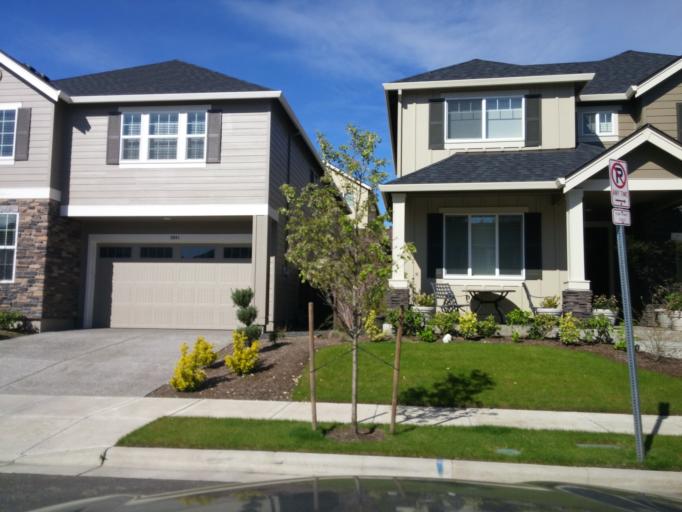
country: US
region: Oregon
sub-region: Washington County
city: West Haven
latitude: 45.5419
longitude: -122.7852
